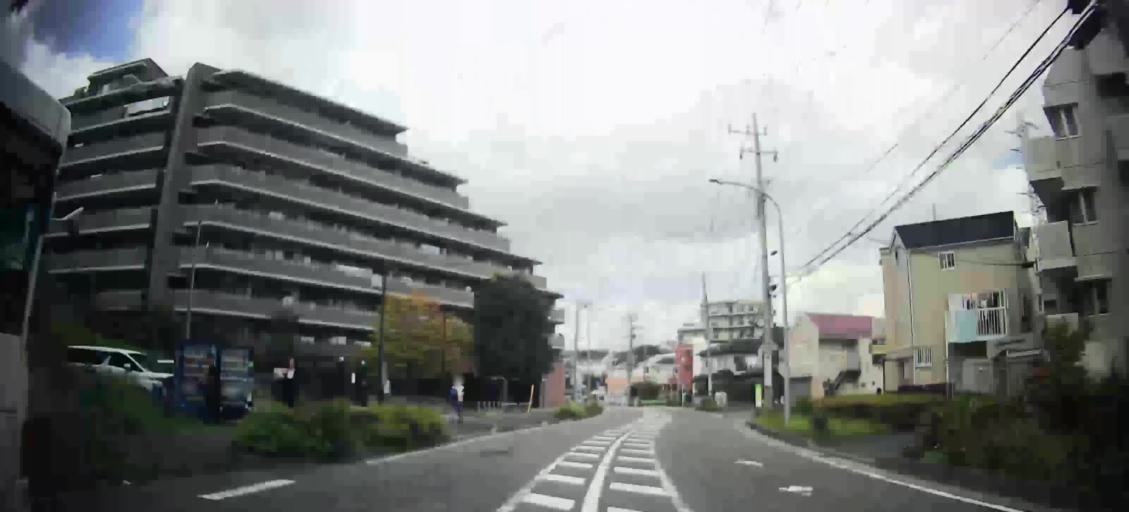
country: JP
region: Kanagawa
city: Minami-rinkan
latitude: 35.4824
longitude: 139.5470
